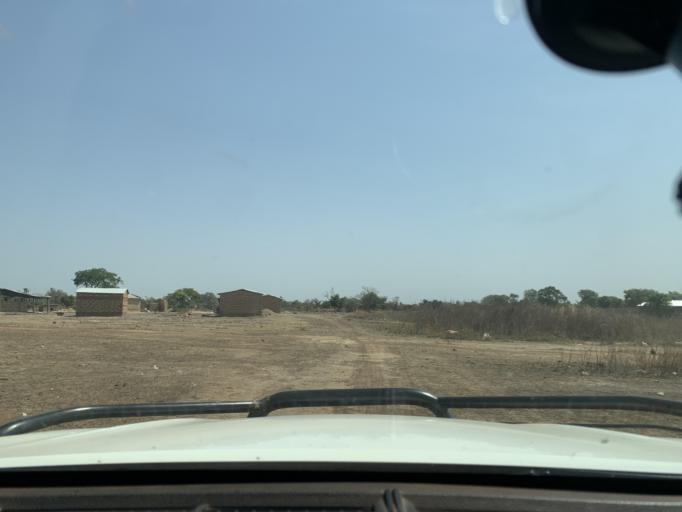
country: ML
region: Sikasso
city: Kolondieba
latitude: 10.8418
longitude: -6.8038
